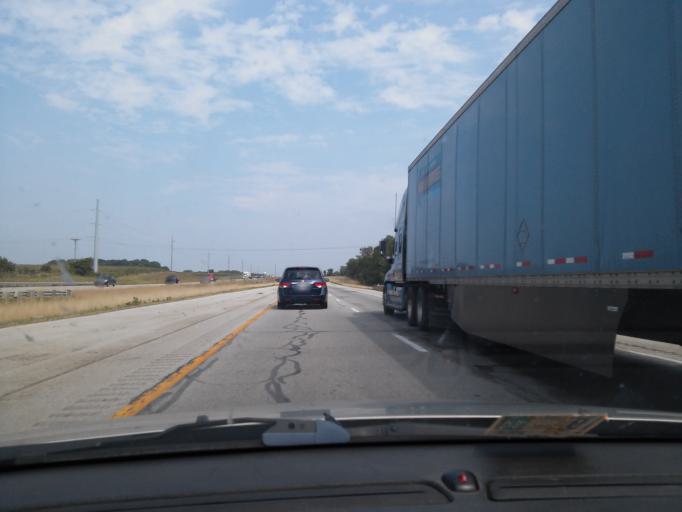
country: US
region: Ohio
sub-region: Preble County
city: Lewisburg
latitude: 39.8360
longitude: -84.5800
